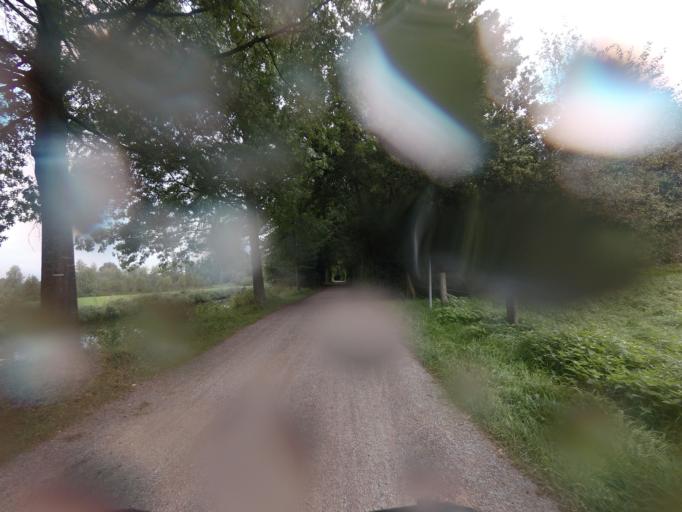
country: DE
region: North Rhine-Westphalia
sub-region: Regierungsbezirk Munster
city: Gronau
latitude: 52.2028
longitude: 7.0184
